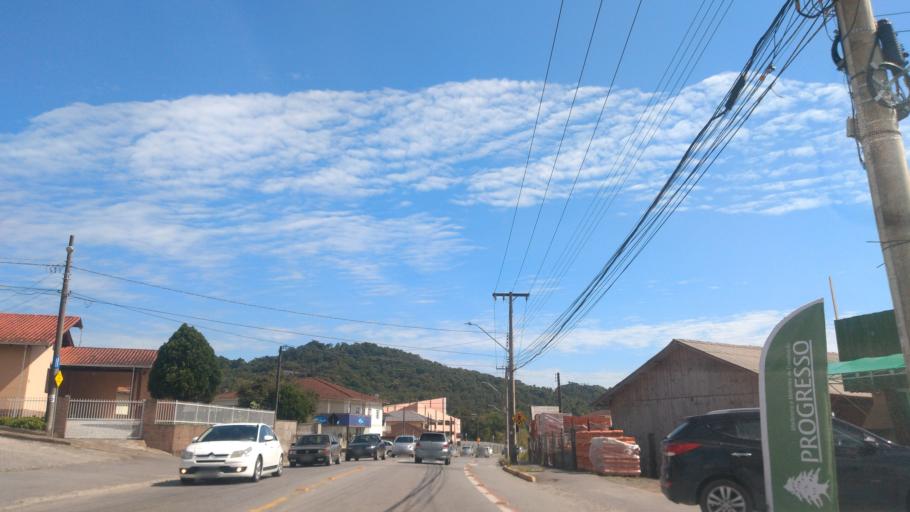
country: BR
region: Santa Catarina
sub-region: Joinville
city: Joinville
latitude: -26.2489
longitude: -48.8214
